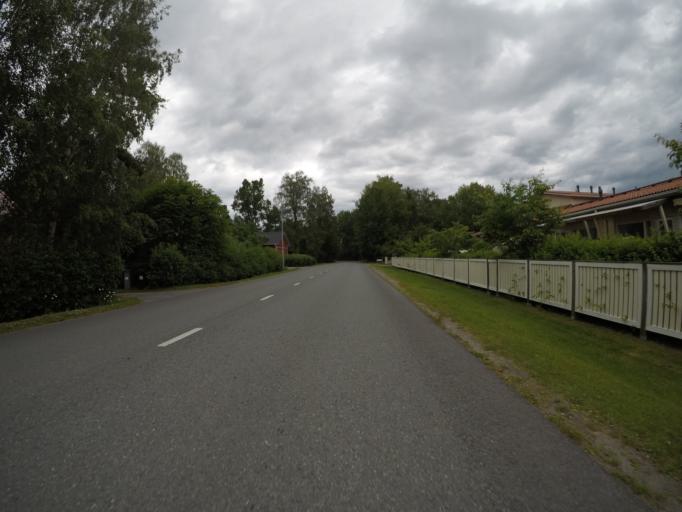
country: FI
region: Haeme
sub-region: Haemeenlinna
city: Haemeenlinna
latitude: 60.9802
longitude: 24.4654
